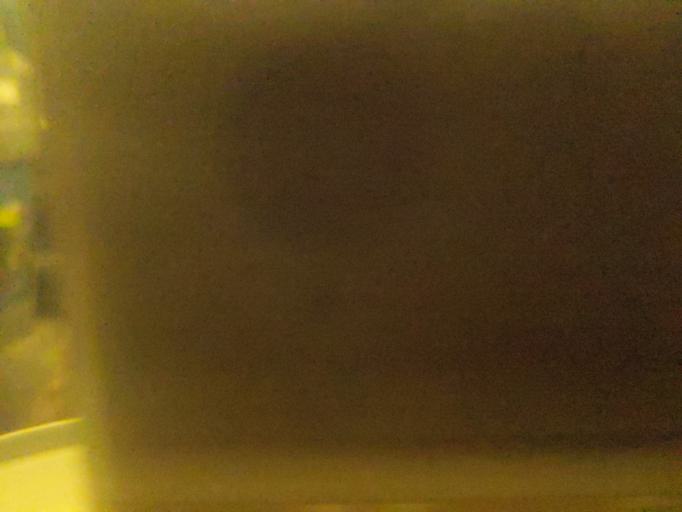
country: JP
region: Shiga Prefecture
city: Otsu-shi
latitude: 34.9738
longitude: 135.8782
